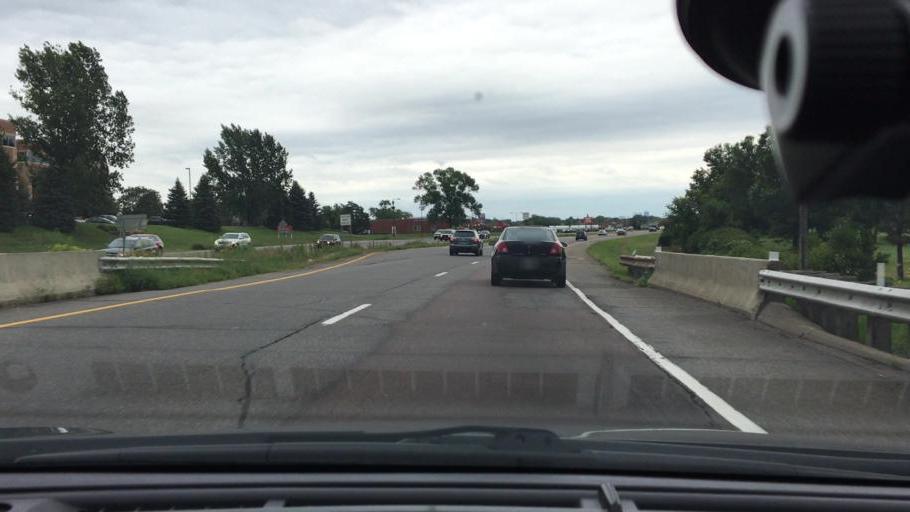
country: US
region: Minnesota
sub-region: Hennepin County
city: Golden Valley
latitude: 44.9847
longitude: -93.3882
